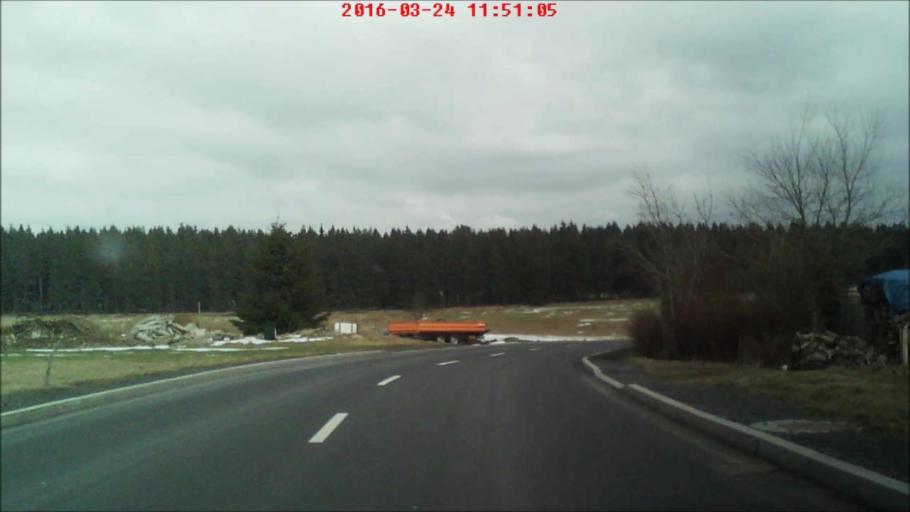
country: DE
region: Thuringia
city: Steinheid
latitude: 50.4695
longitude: 11.0444
